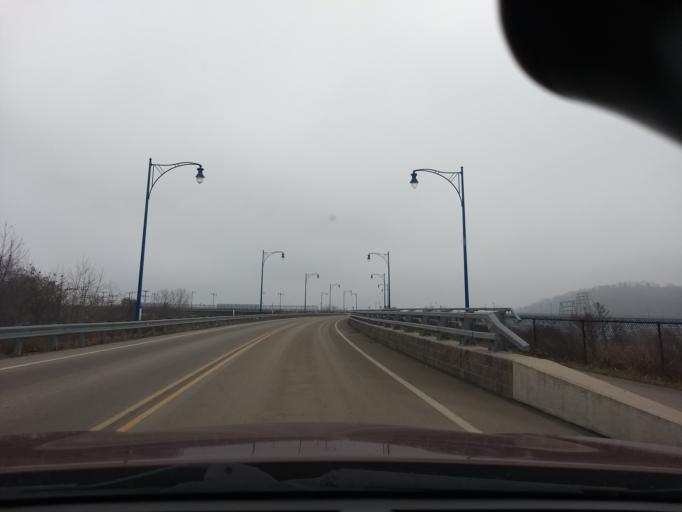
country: US
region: Pennsylvania
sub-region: Allegheny County
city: Rankin
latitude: 40.4106
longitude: -79.8820
